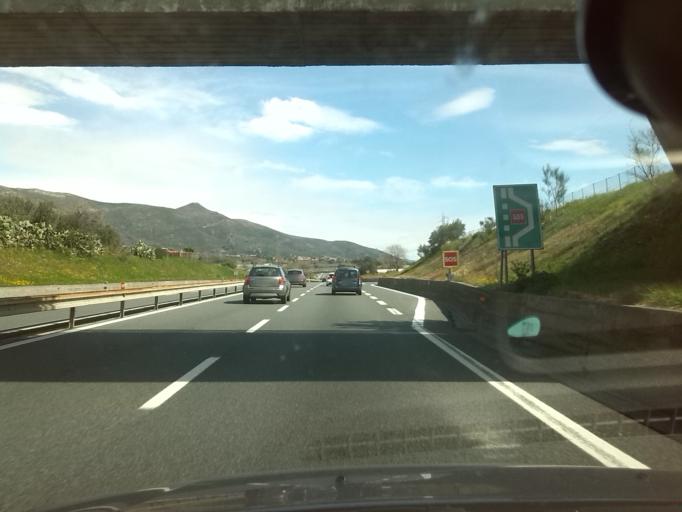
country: IT
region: Liguria
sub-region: Provincia di Savona
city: Campochiesa
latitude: 44.0707
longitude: 8.1815
